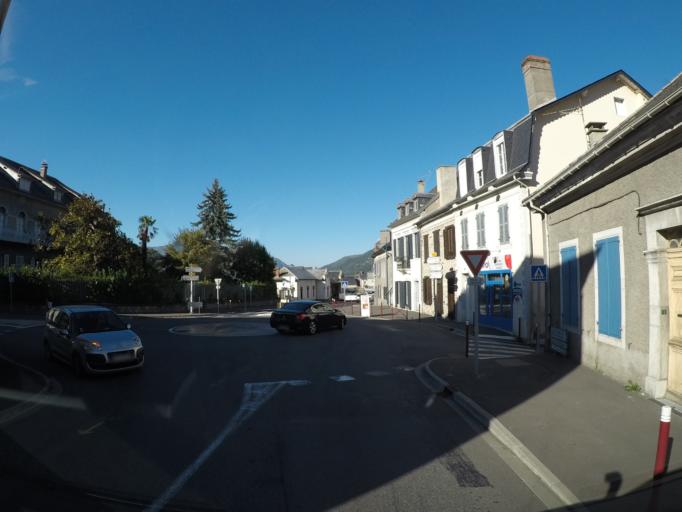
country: FR
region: Midi-Pyrenees
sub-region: Departement des Hautes-Pyrenees
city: Pierrefitte-Nestalas
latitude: 42.9576
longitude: -0.0750
